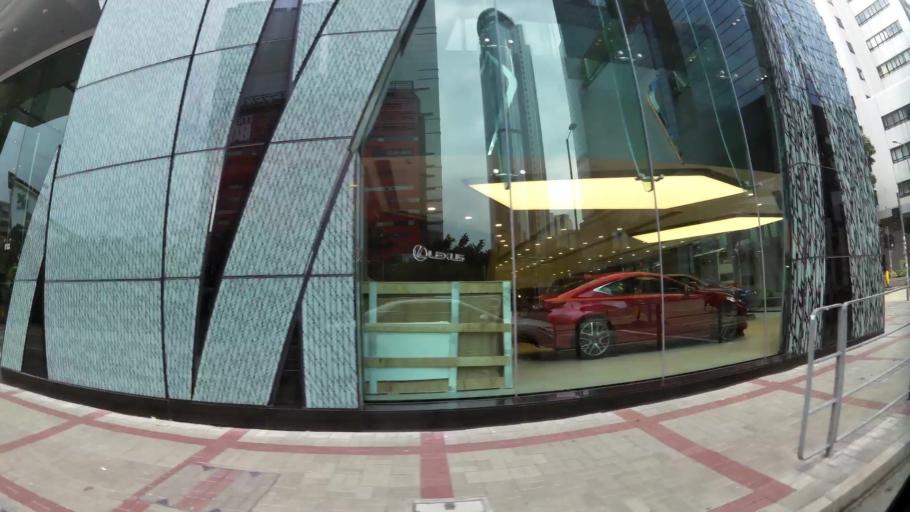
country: HK
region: Kowloon City
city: Kowloon
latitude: 22.3218
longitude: 114.2087
